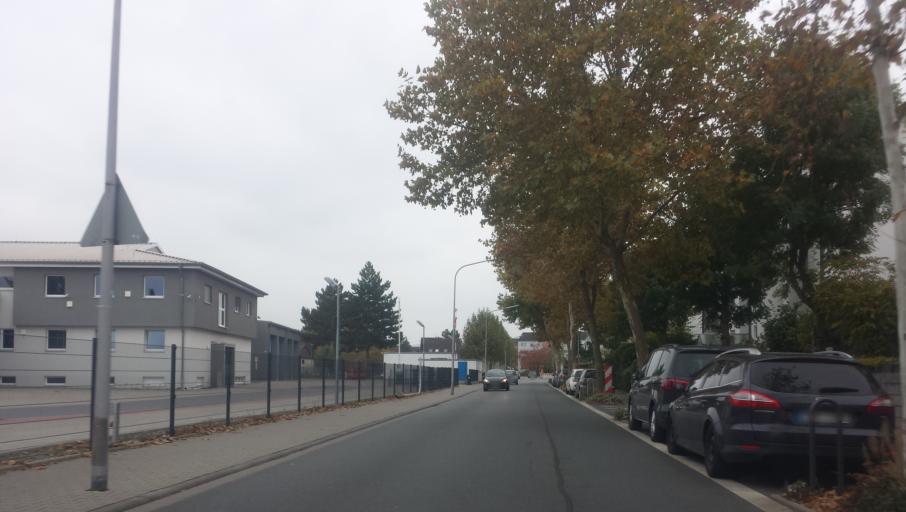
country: DE
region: Hesse
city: Pfungstadt
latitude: 49.8026
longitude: 8.6058
